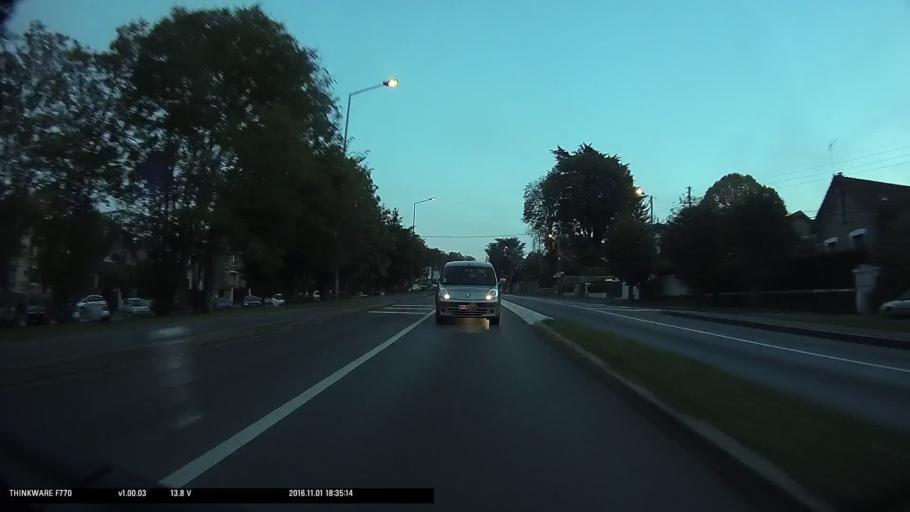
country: FR
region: Ile-de-France
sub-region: Departement de l'Essonne
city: Villemoisson-sur-Orge
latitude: 48.6648
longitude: 2.3401
